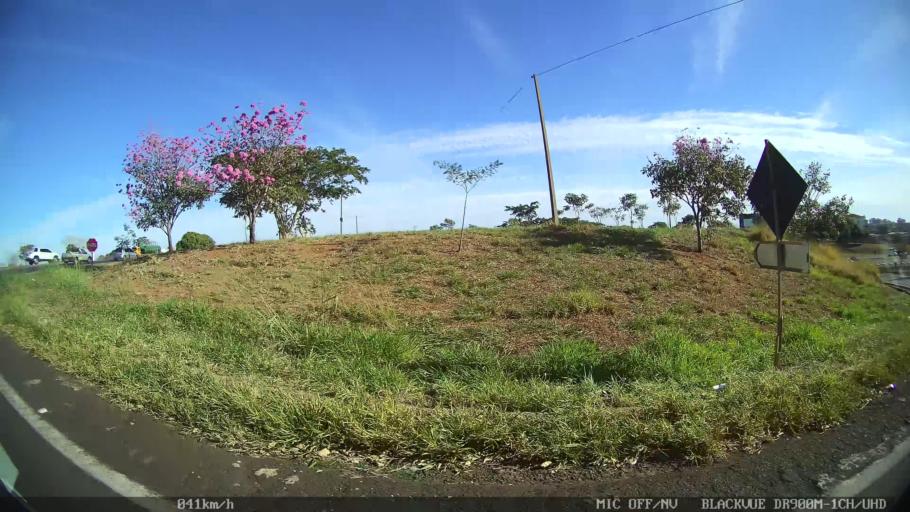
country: BR
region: Sao Paulo
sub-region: Sao Jose Do Rio Preto
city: Sao Jose do Rio Preto
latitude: -20.8293
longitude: -49.3619
